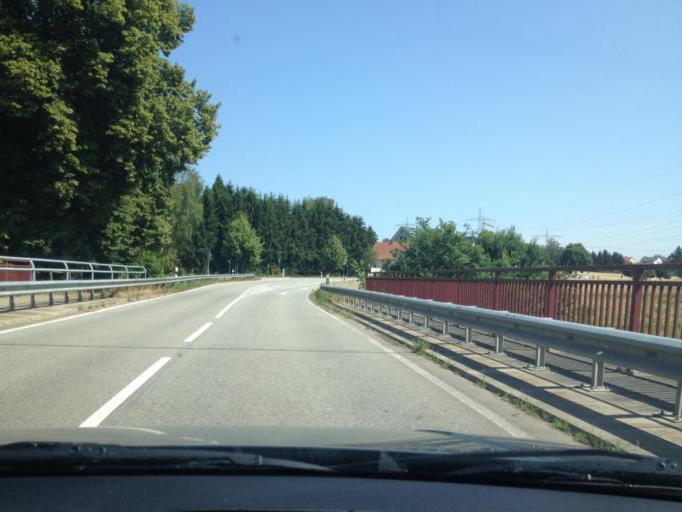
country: DE
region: Rheinland-Pfalz
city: Hutschenhausen
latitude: 49.4158
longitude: 7.4599
